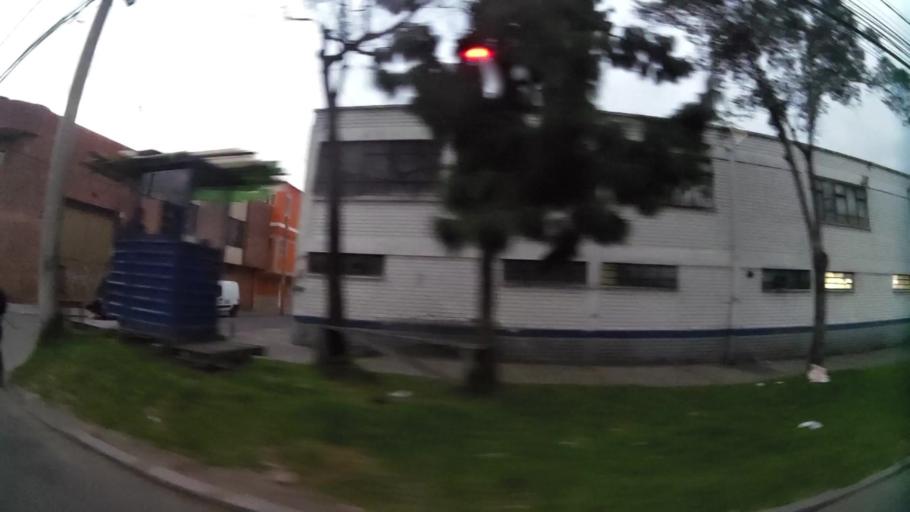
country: CO
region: Bogota D.C.
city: Bogota
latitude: 4.6213
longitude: -74.0815
